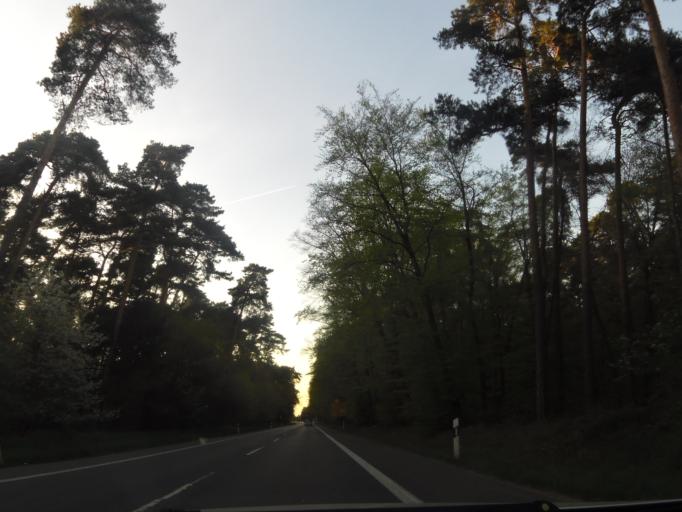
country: DE
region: Hesse
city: Weiterstadt
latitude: 49.9078
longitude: 8.6145
